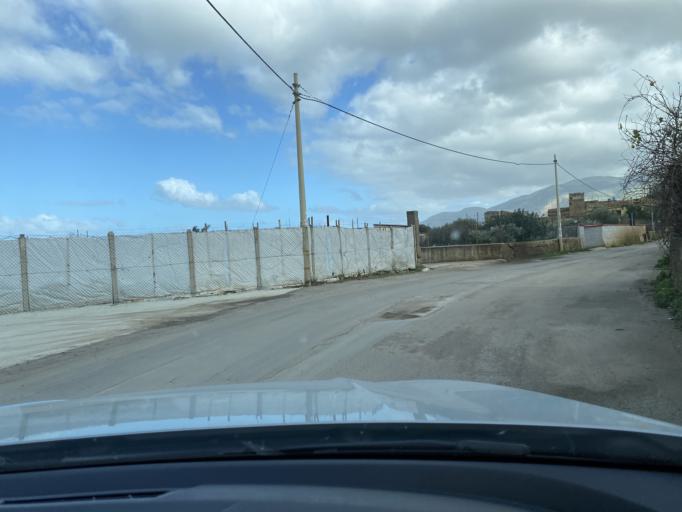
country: IT
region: Sicily
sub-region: Palermo
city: Carini
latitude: 38.1493
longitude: 13.1653
